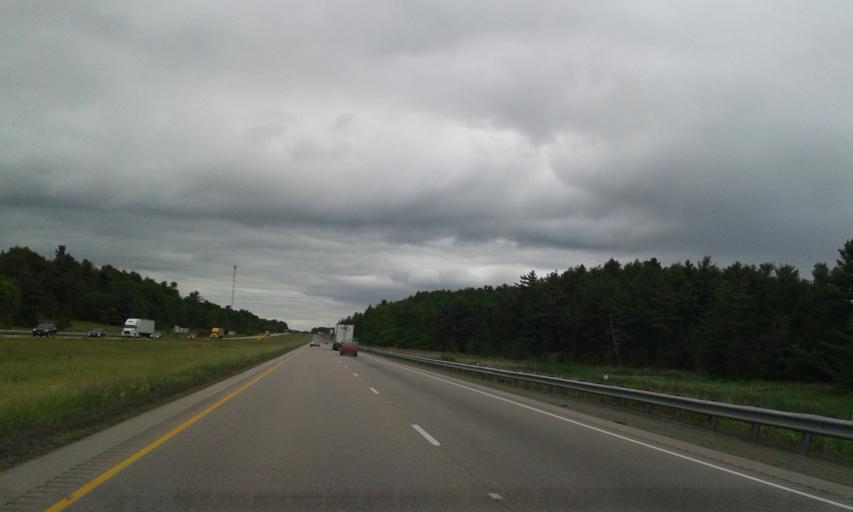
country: US
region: New York
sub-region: Jefferson County
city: Alexandria Bay
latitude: 44.4938
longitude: -75.8500
